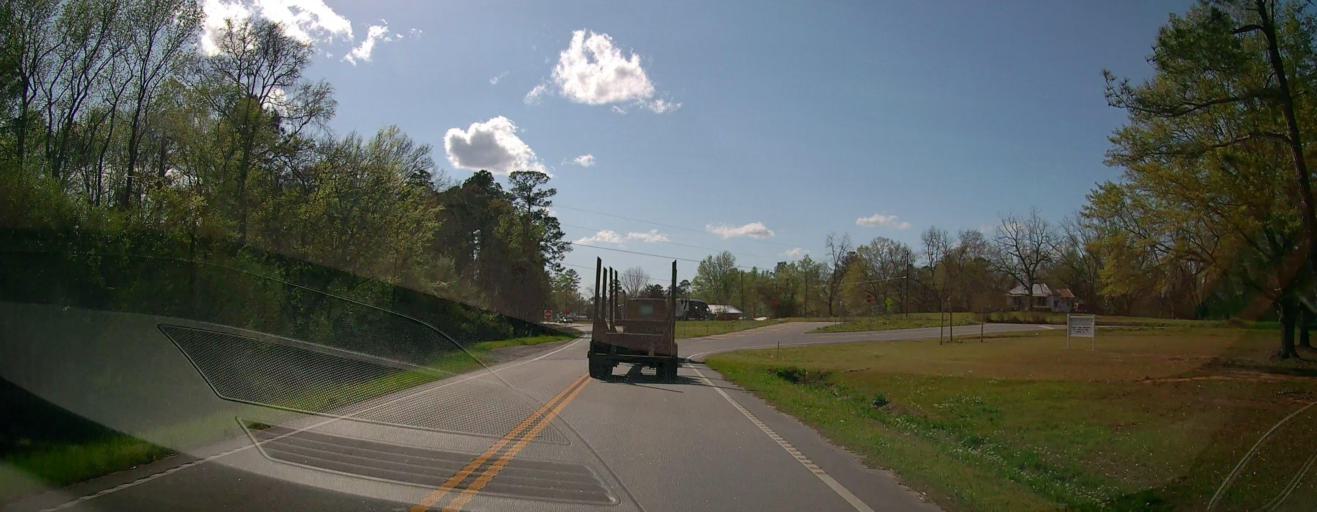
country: US
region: Georgia
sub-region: Baldwin County
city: Hardwick
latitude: 33.0805
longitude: -83.1604
